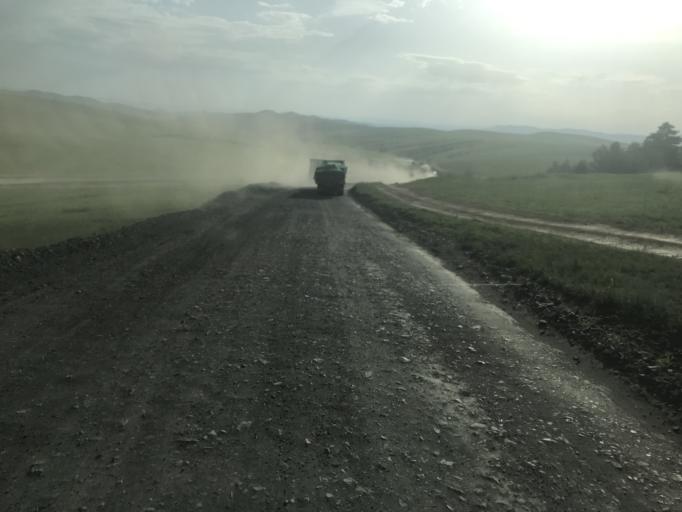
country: MN
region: Central Aimak
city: Javhlant
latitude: 48.6491
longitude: 106.0960
